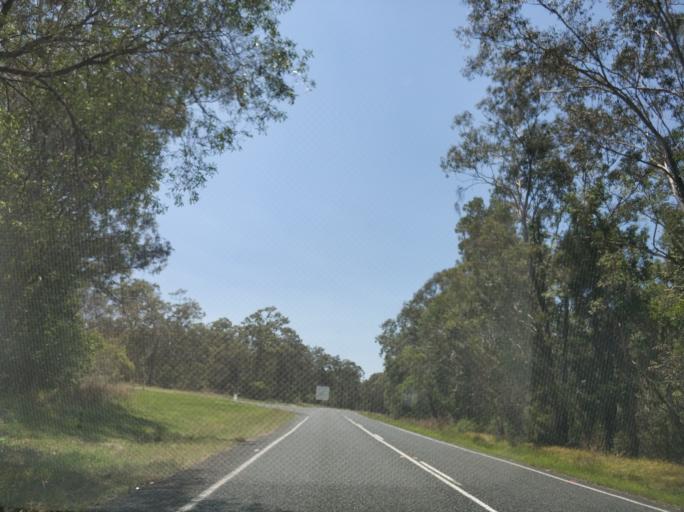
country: AU
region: Queensland
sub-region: Gladstone
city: Toolooa
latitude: -24.3253
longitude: 151.5729
